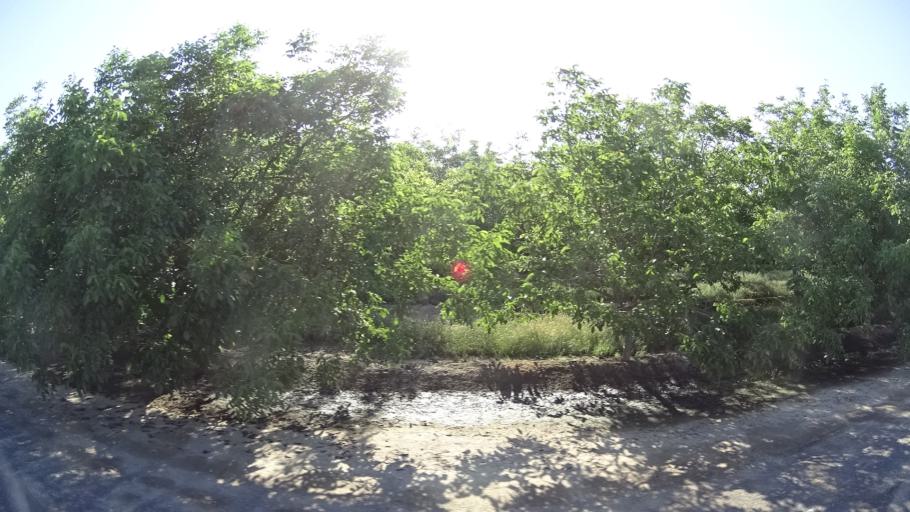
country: US
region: California
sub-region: Fresno County
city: Laton
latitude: 36.4096
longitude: -119.7133
